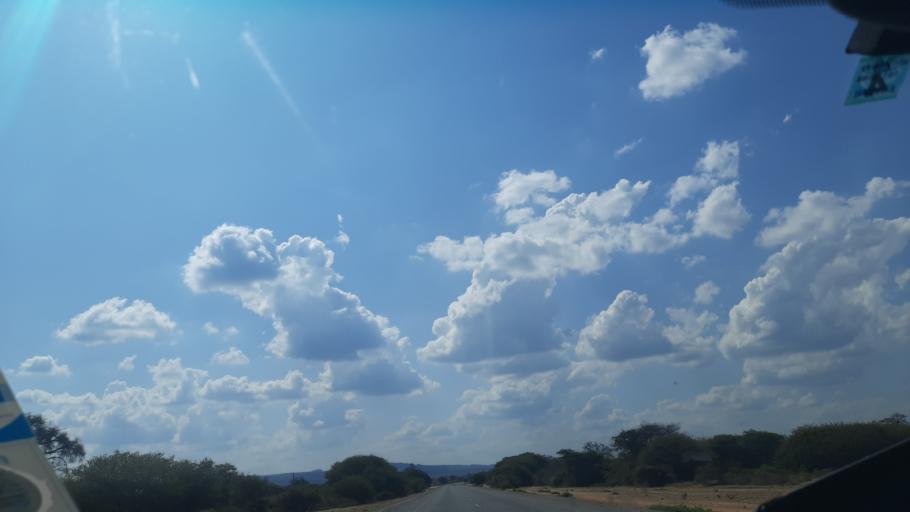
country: TZ
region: Singida
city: Kilimatinde
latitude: -5.8357
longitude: 35.0640
